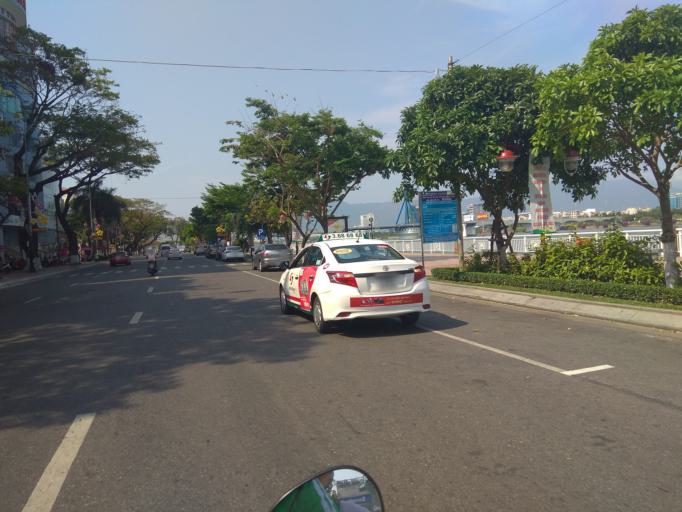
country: VN
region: Da Nang
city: Da Nang
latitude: 16.0690
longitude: 108.2250
